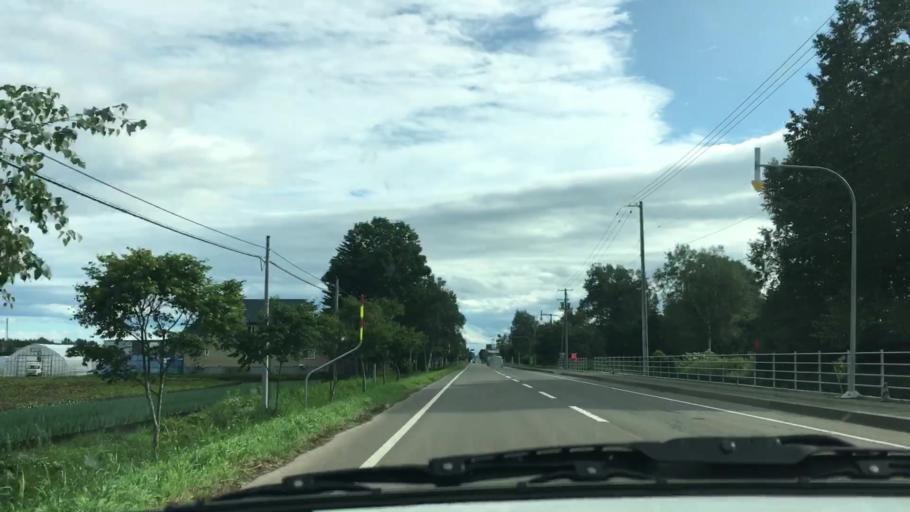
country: JP
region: Hokkaido
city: Otofuke
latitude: 43.2437
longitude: 143.2975
